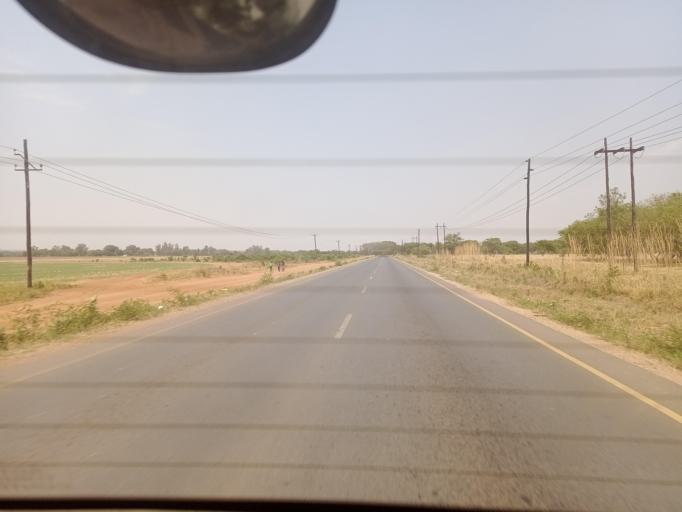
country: ZM
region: Lusaka
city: Lusaka
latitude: -15.2705
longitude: 28.4122
